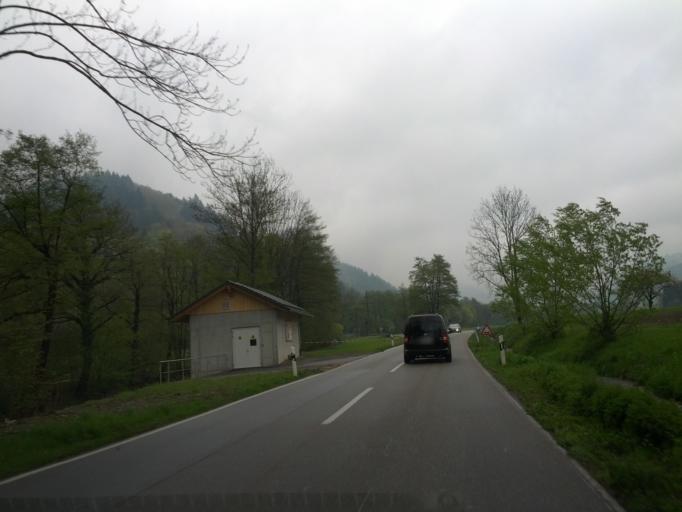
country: DE
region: Baden-Wuerttemberg
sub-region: Freiburg Region
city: Muenstertal/Schwarzwald
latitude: 47.8671
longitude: 7.7457
